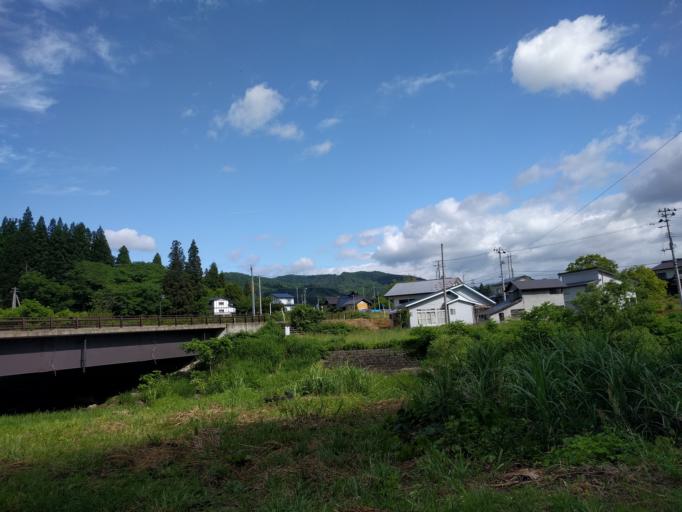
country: JP
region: Fukushima
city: Kitakata
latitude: 37.4320
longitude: 139.8135
